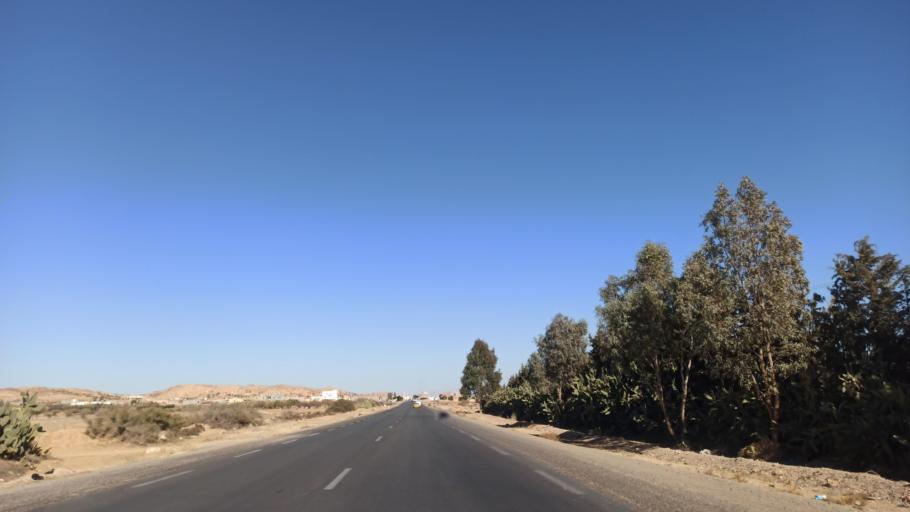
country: TN
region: Sidi Bu Zayd
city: Bi'r al Hufayy
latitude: 34.9078
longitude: 9.1795
